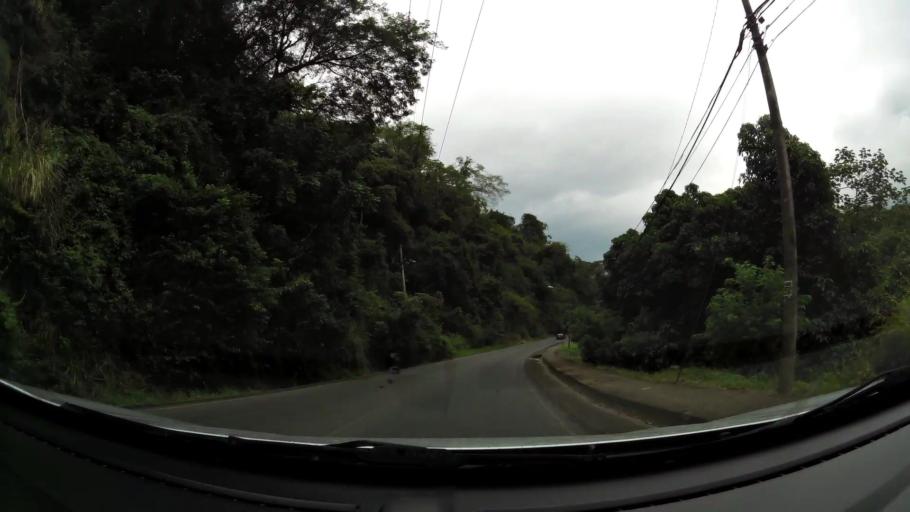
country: CR
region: Puntarenas
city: Esparza
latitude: 9.9954
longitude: -84.7023
